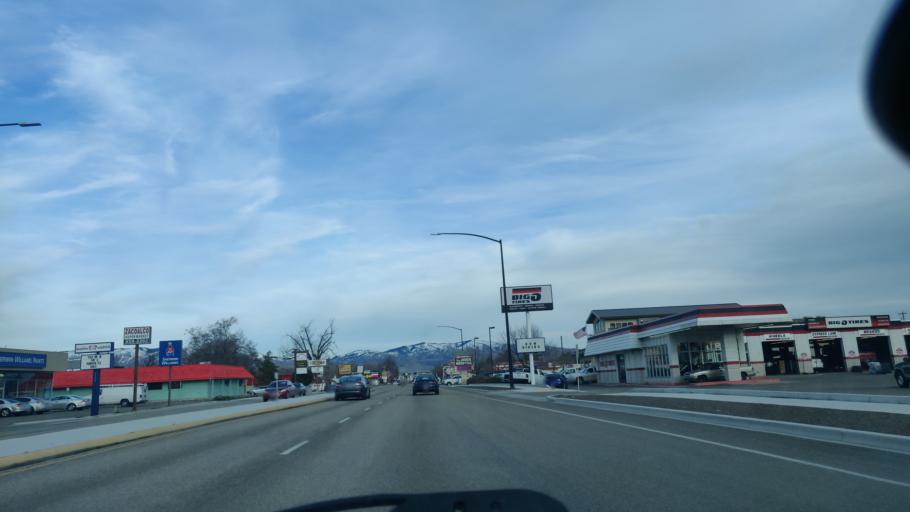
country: US
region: Idaho
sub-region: Ada County
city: Garden City
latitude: 43.6192
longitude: -116.2721
